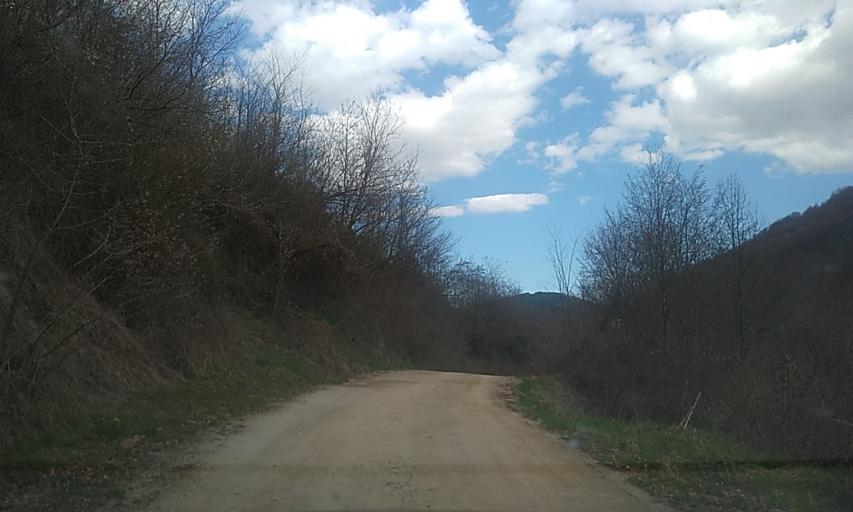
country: MK
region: Kriva Palanka
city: Kriva Palanka
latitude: 42.3409
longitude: 22.3679
